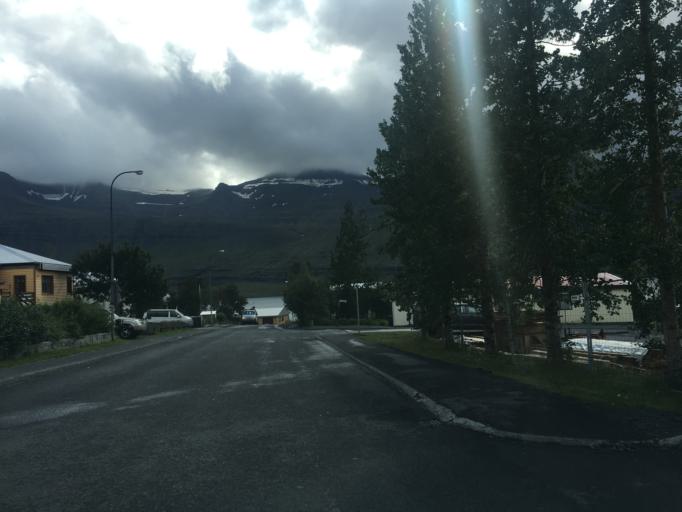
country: IS
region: East
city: Reydarfjoerdur
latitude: 65.0338
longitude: -14.2139
